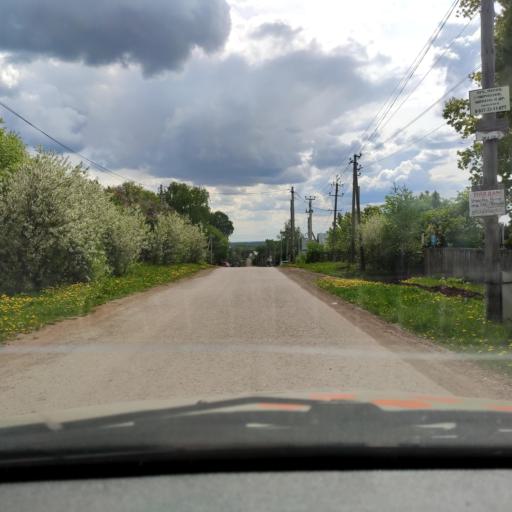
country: RU
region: Bashkortostan
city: Avdon
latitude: 54.6486
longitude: 55.7034
